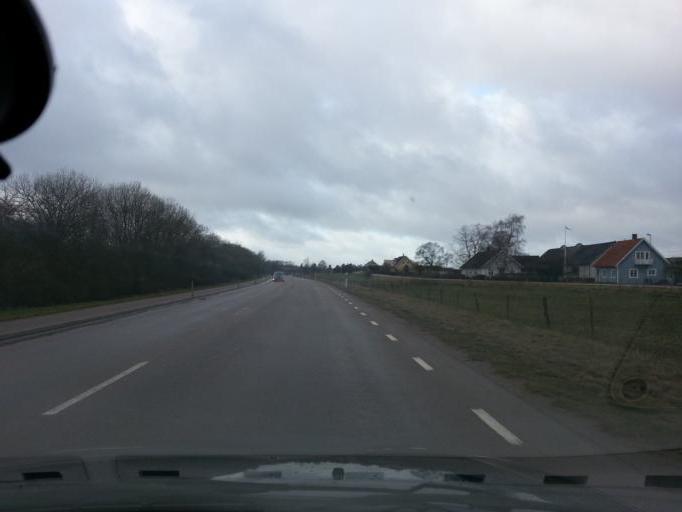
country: SE
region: Skane
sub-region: Astorps Kommun
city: Astorp
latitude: 56.1366
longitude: 12.9730
